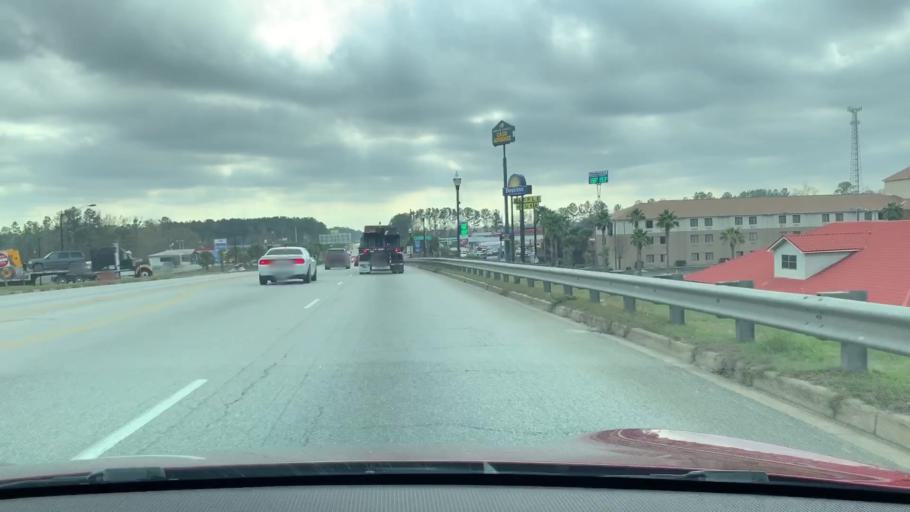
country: US
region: South Carolina
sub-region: Jasper County
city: Hardeeville
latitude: 32.2722
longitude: -81.0806
